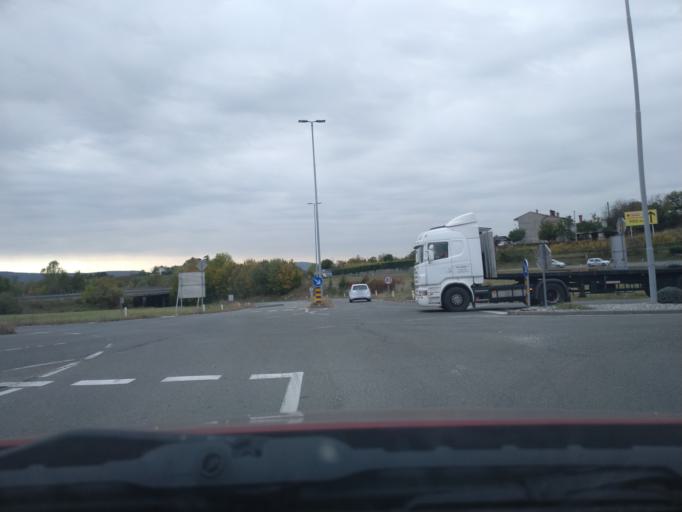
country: SI
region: Sempeter-Vrtojba
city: Sempeter pri Gorici
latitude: 45.9222
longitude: 13.6518
